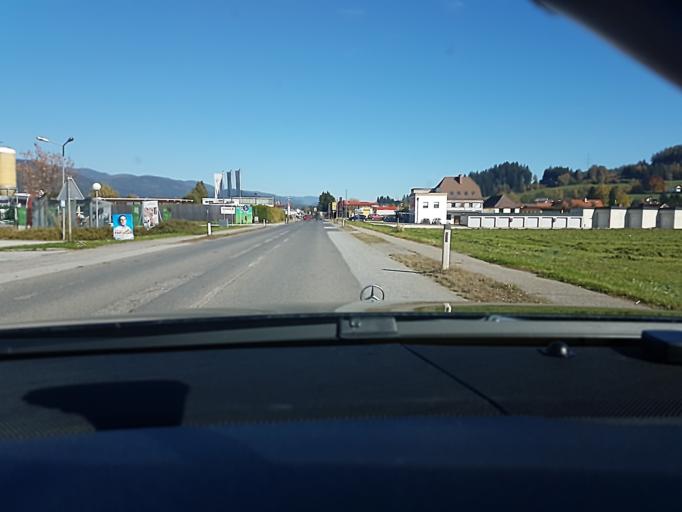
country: AT
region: Styria
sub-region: Politischer Bezirk Bruck-Muerzzuschlag
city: Mitterdorf im Muerztal
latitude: 47.5310
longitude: 15.5083
